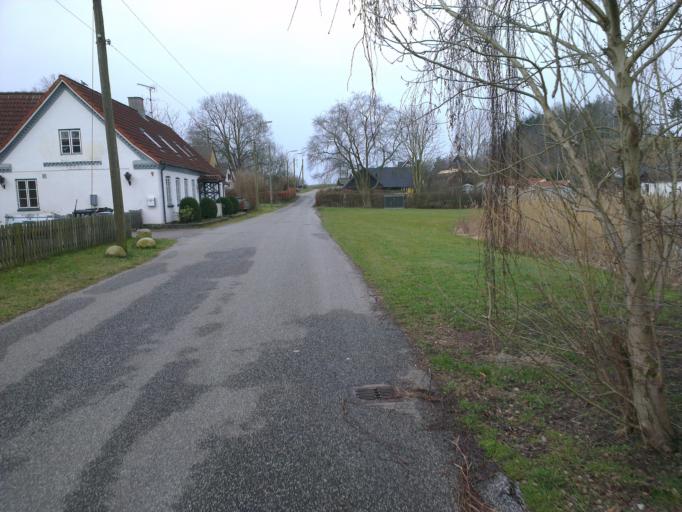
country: DK
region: Zealand
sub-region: Lejre Kommune
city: Ejby
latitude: 55.7422
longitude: 11.8775
